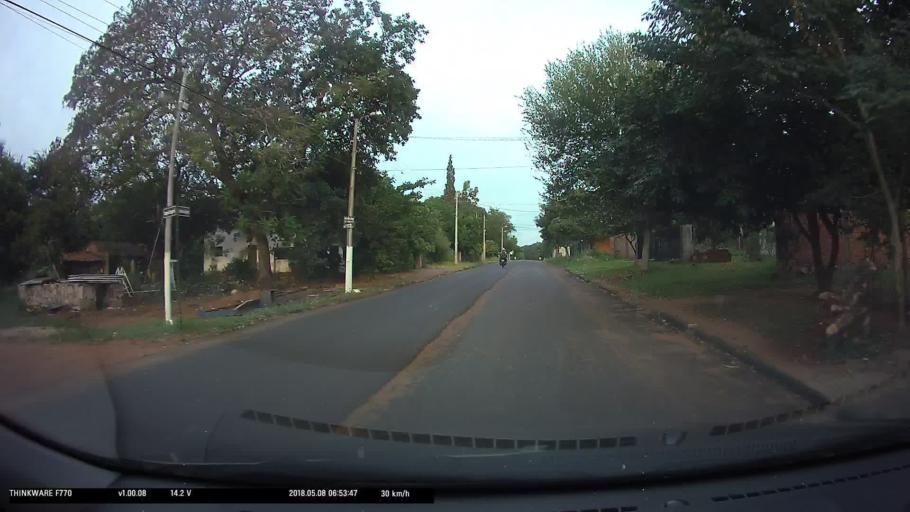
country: PY
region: Central
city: Limpio
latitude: -25.2354
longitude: -57.4721
